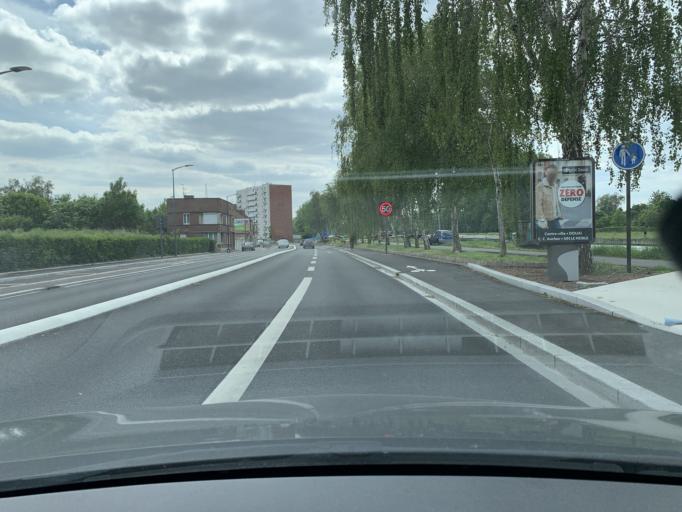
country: FR
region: Nord-Pas-de-Calais
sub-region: Departement du Nord
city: Douai
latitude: 50.3711
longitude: 3.0654
